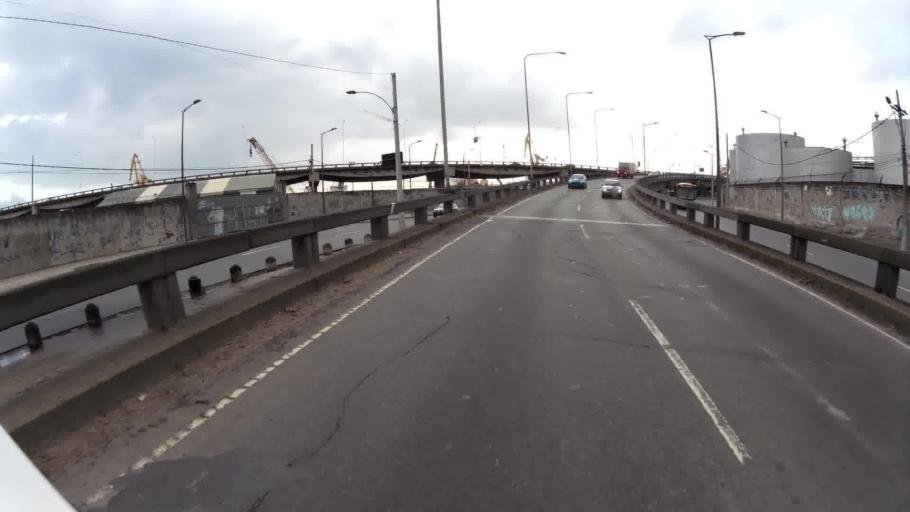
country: BR
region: Rio de Janeiro
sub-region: Rio De Janeiro
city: Rio de Janeiro
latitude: -22.8888
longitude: -43.2176
